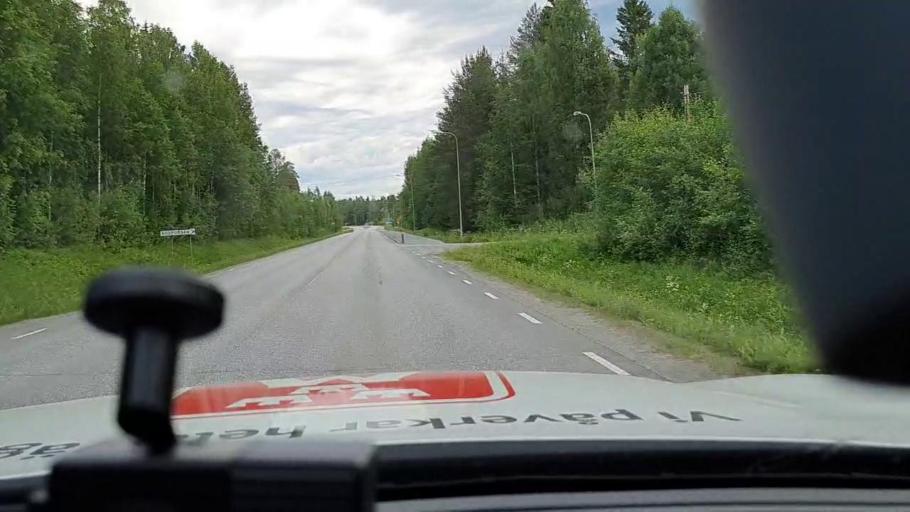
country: SE
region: Norrbotten
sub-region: Bodens Kommun
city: Boden
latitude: 65.8110
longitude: 21.6518
